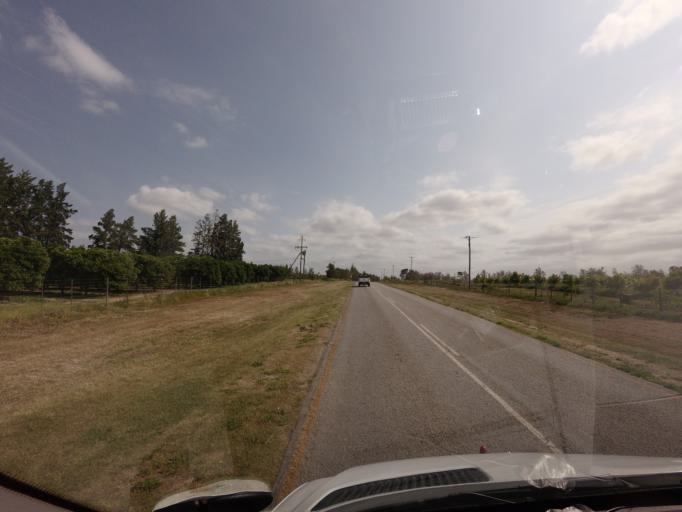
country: ZA
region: Eastern Cape
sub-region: Cacadu District Municipality
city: Kirkwood
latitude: -33.5671
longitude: 25.6801
